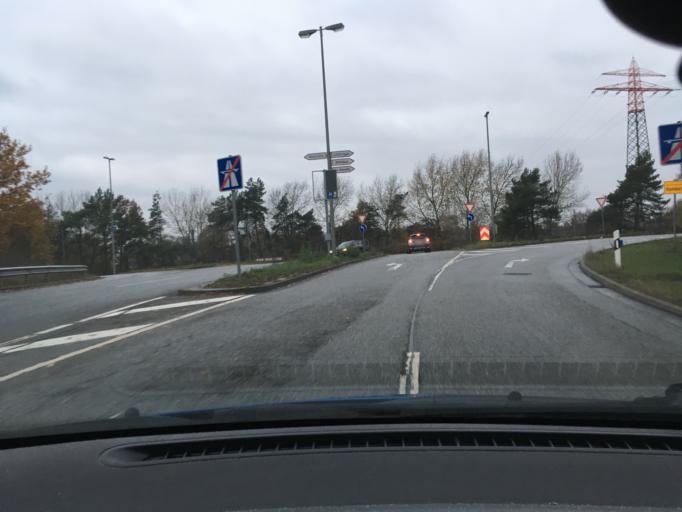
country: DE
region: Hamburg
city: Bergedorf
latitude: 53.4725
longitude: 10.1769
